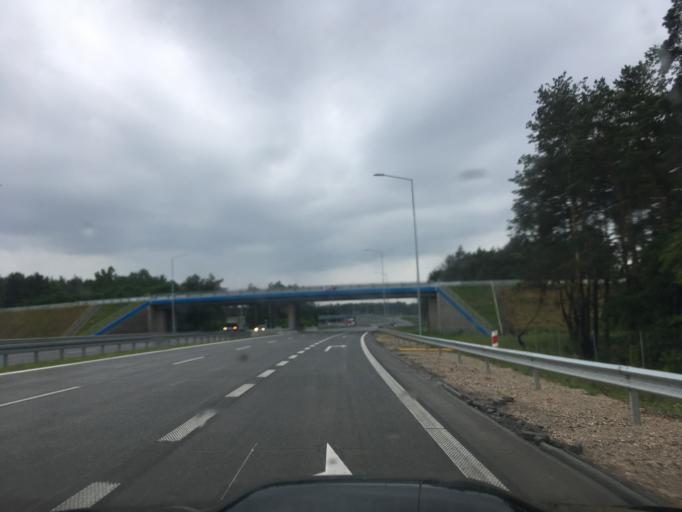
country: PL
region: Masovian Voivodeship
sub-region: Powiat piaseczynski
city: Gora Kalwaria
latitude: 51.9696
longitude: 21.2039
